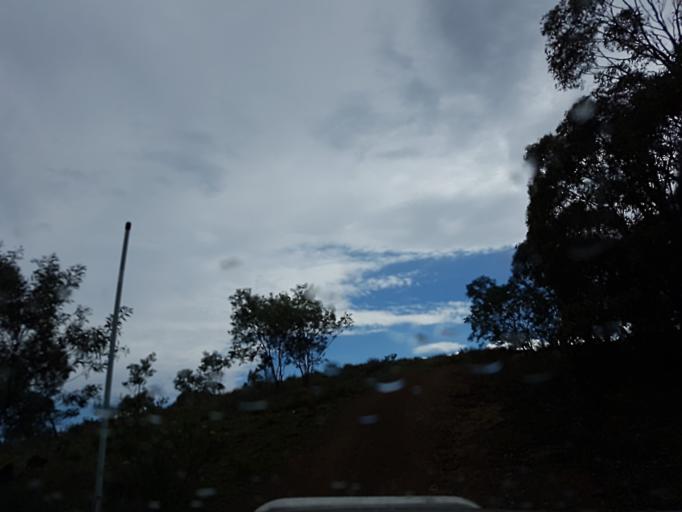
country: AU
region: New South Wales
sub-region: Snowy River
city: Jindabyne
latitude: -36.9105
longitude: 148.3372
